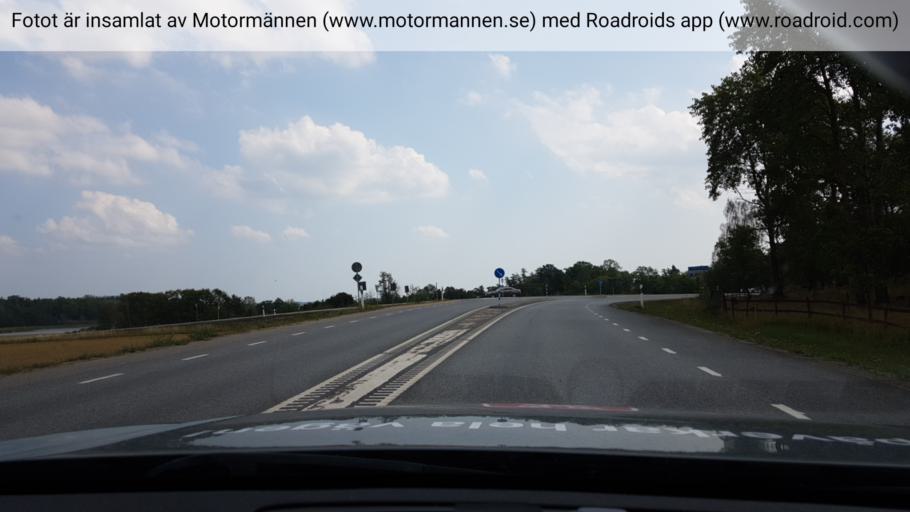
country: SE
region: Stockholm
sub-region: Sodertalje Kommun
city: Pershagen
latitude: 59.0860
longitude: 17.6035
